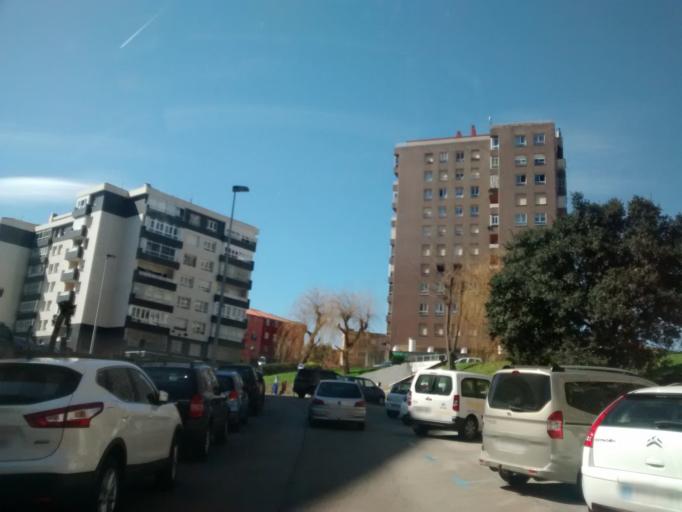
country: ES
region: Cantabria
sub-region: Provincia de Cantabria
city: Santander
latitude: 43.4650
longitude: -3.8136
